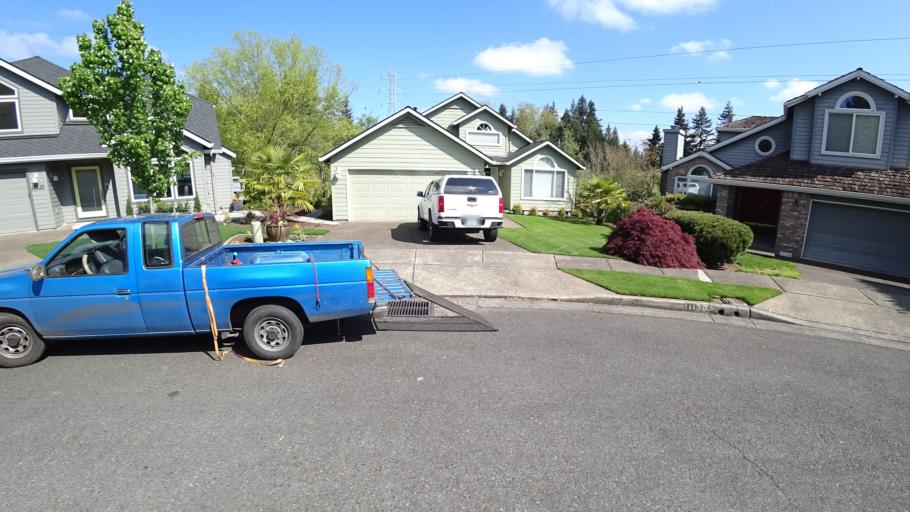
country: US
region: Oregon
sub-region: Washington County
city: King City
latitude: 45.4393
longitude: -122.8345
